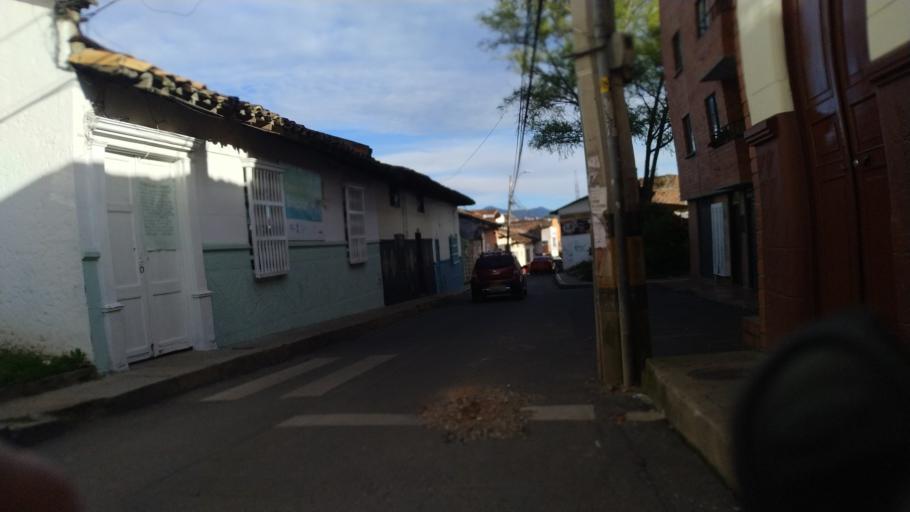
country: CO
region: Antioquia
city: Rionegro
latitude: 6.1506
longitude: -75.3754
